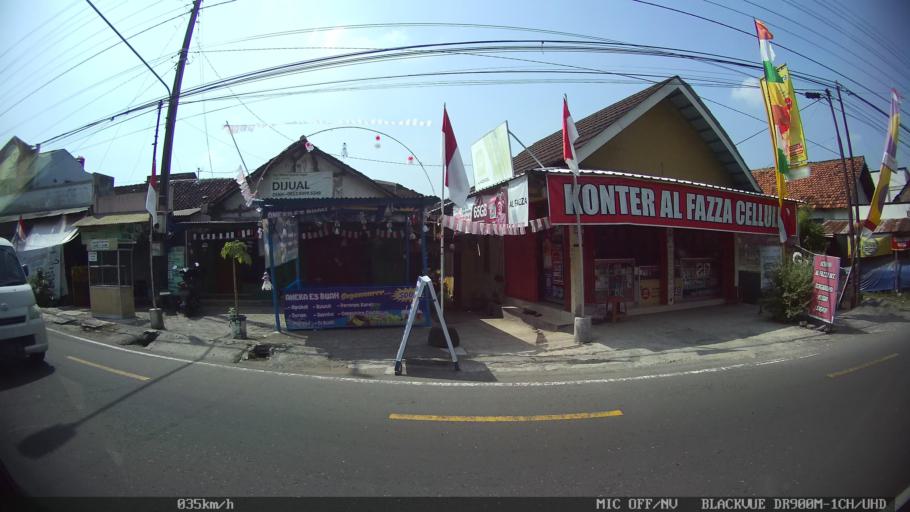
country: ID
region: Daerah Istimewa Yogyakarta
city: Yogyakarta
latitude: -7.8119
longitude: 110.3926
